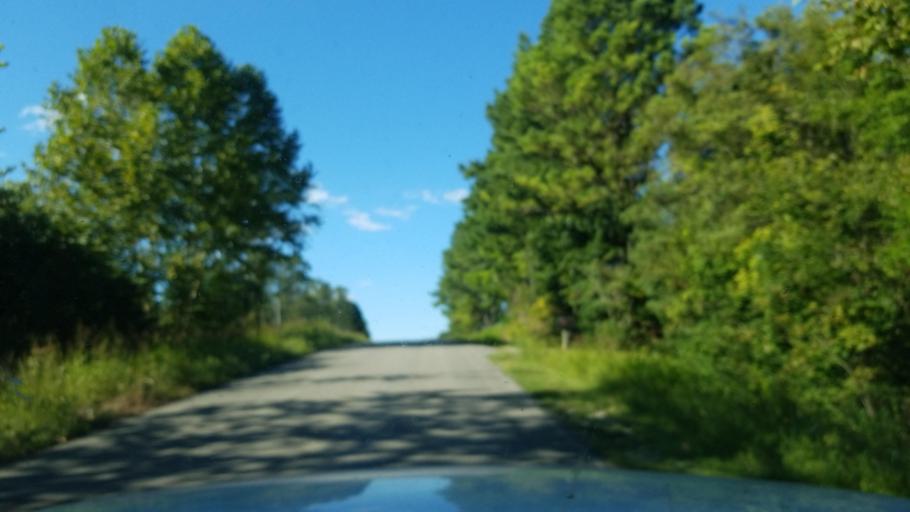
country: US
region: Illinois
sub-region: Hardin County
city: Elizabethtown
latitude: 37.5829
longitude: -88.3655
